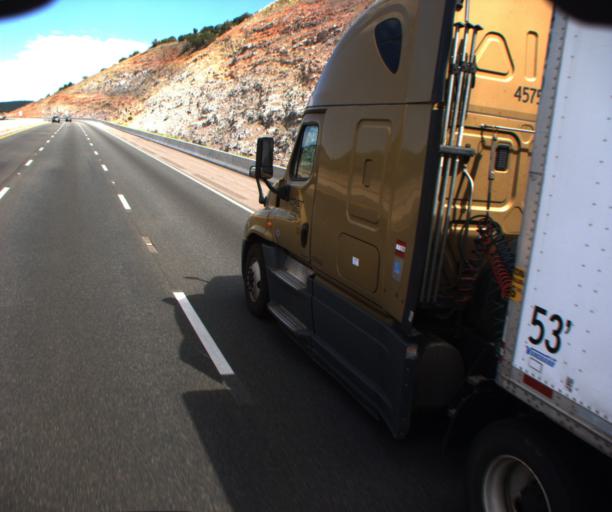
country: US
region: Arizona
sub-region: Yavapai County
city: Camp Verde
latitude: 34.5317
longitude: -111.9548
